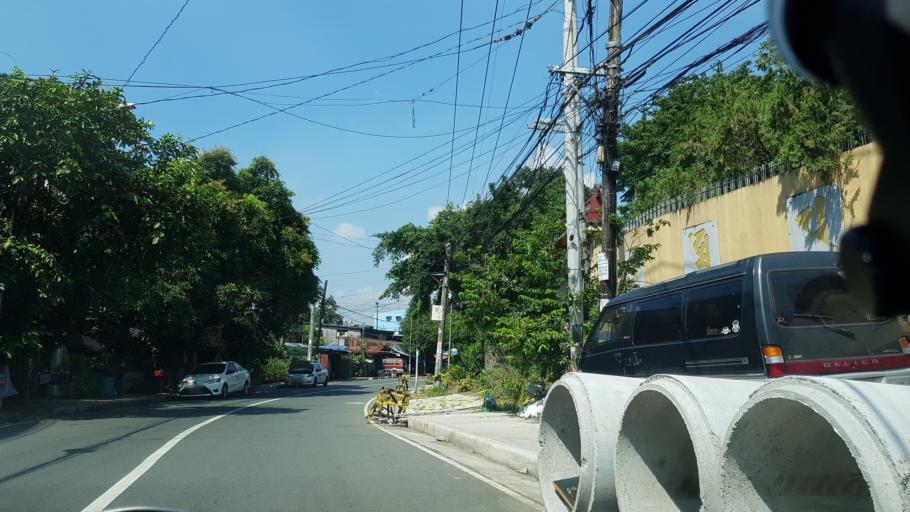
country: PH
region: Metro Manila
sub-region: San Juan
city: San Juan
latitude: 14.6187
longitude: 121.0451
